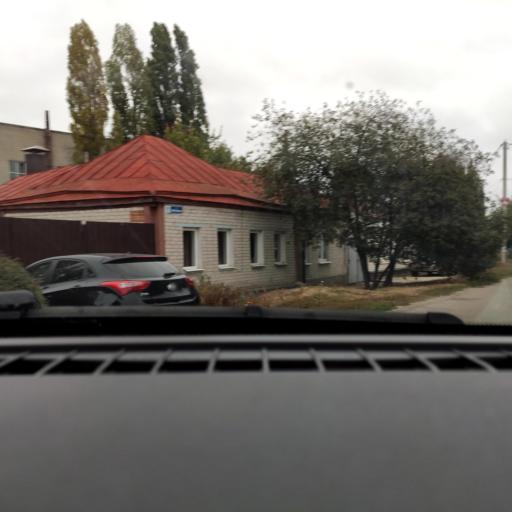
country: RU
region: Voronezj
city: Voronezh
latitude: 51.6703
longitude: 39.2637
